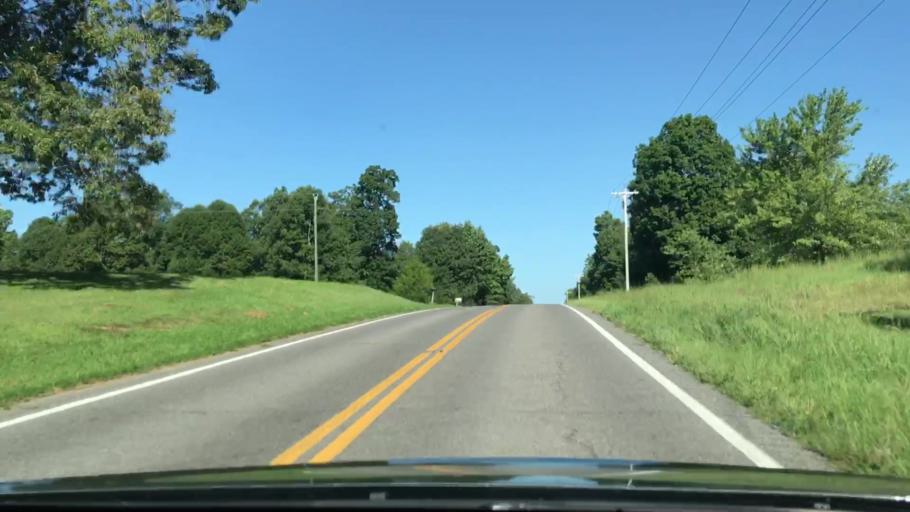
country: US
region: Kentucky
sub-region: Graves County
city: Mayfield
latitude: 36.7746
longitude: -88.5044
